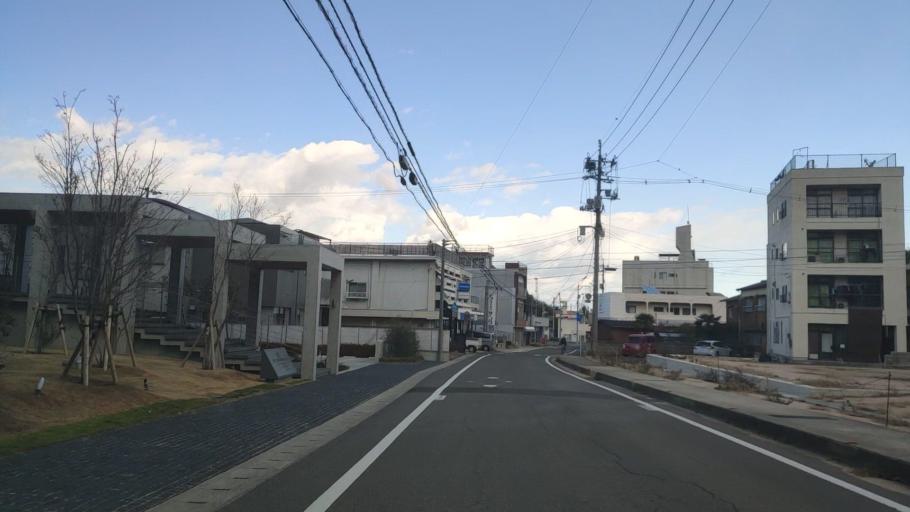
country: JP
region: Hiroshima
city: Innoshima
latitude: 34.2036
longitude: 133.1112
